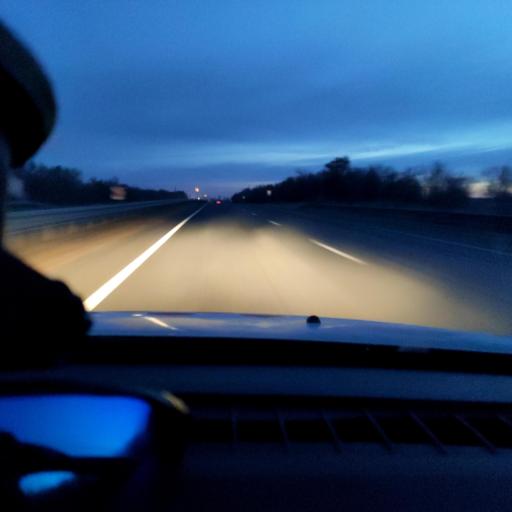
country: RU
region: Samara
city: Novokuybyshevsk
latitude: 53.0433
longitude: 50.0042
